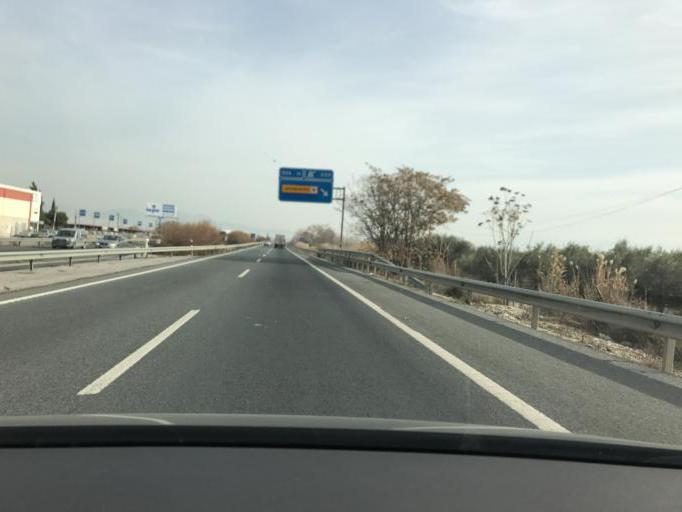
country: ES
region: Andalusia
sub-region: Provincia de Granada
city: Chauchina
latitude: 37.1913
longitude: -3.7608
